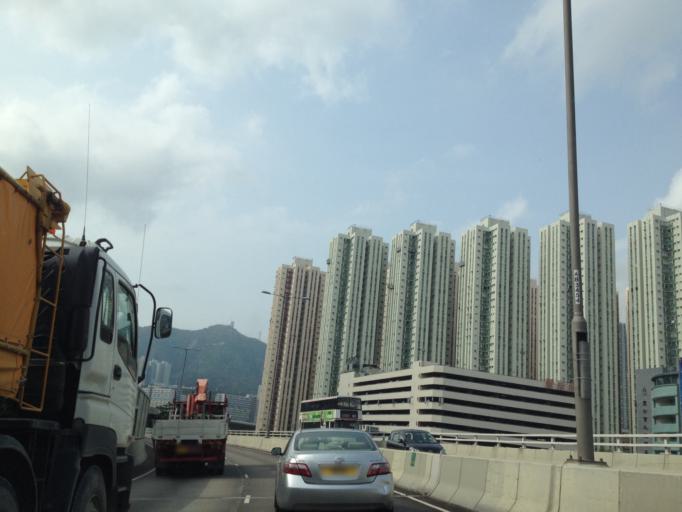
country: HK
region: Kowloon City
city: Kowloon
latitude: 22.3279
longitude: 114.2052
